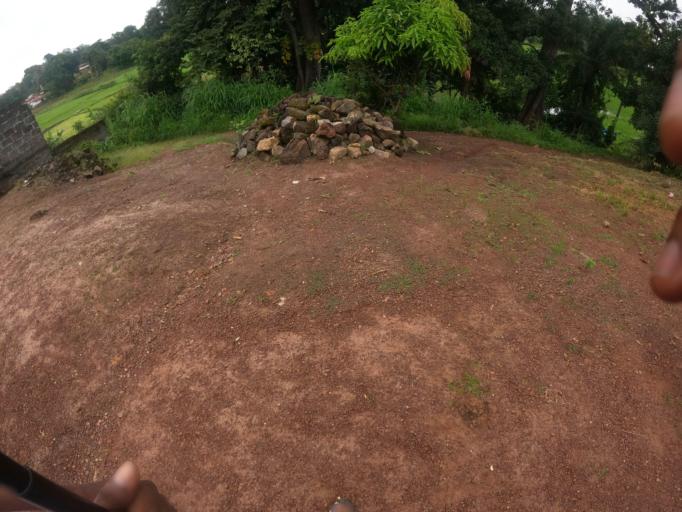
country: SL
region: Northern Province
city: Kamakwie
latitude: 9.5006
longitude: -12.2441
